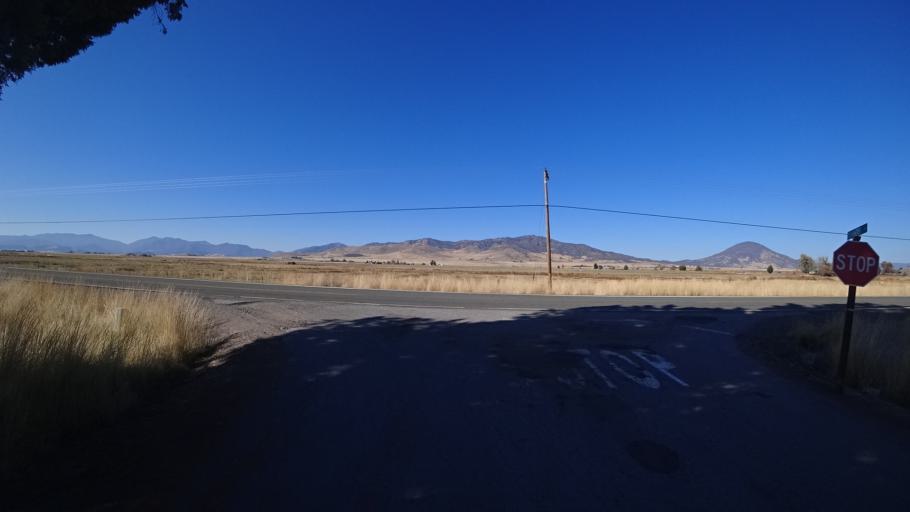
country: US
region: California
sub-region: Siskiyou County
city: Montague
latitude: 41.7659
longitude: -122.4855
